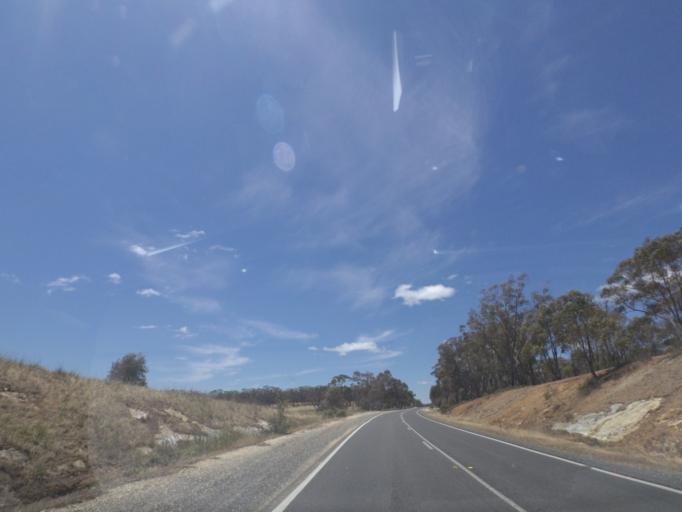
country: AU
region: Victoria
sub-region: Mount Alexander
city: Castlemaine
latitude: -37.1661
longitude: 144.1488
